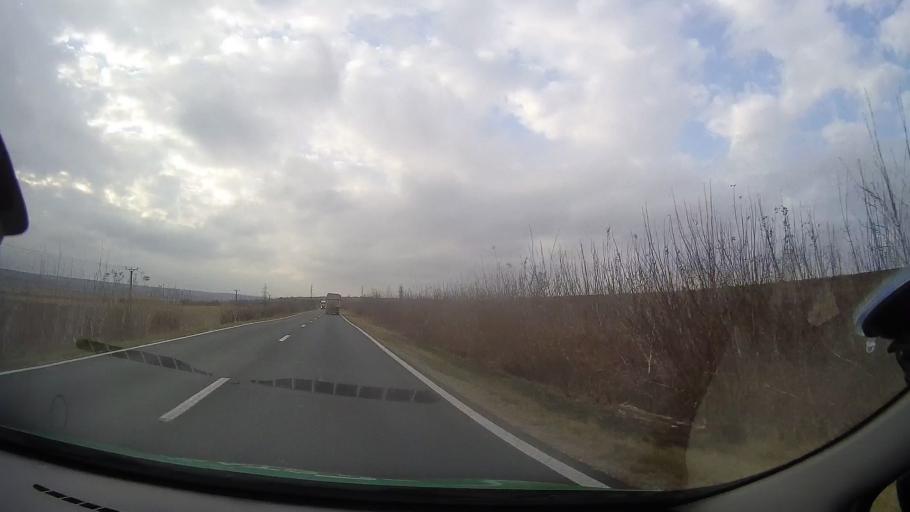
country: RO
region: Constanta
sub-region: Comuna Mircea Voda
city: Satu Nou
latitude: 44.2704
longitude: 28.2082
